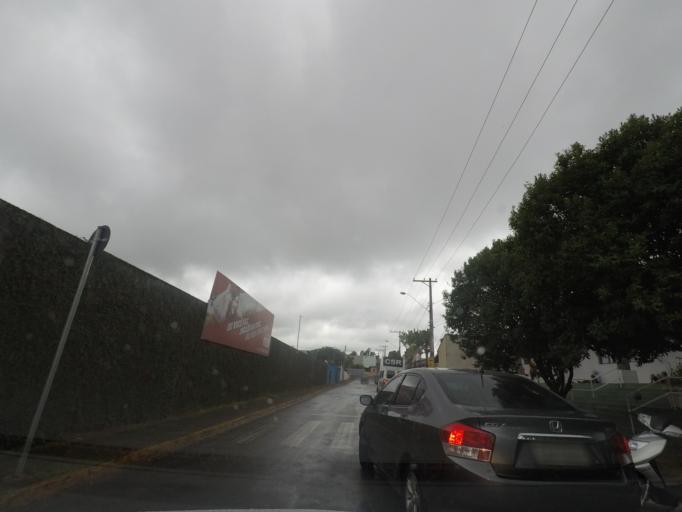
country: BR
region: Sao Paulo
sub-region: Registro
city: Registro
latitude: -24.5075
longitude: -47.8524
